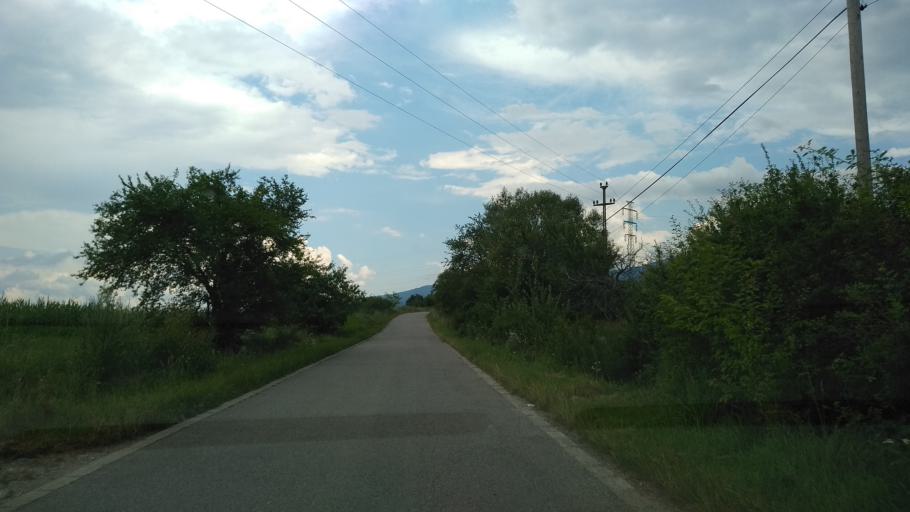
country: RO
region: Hunedoara
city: Salasu de Sus
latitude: 45.5039
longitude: 22.9624
